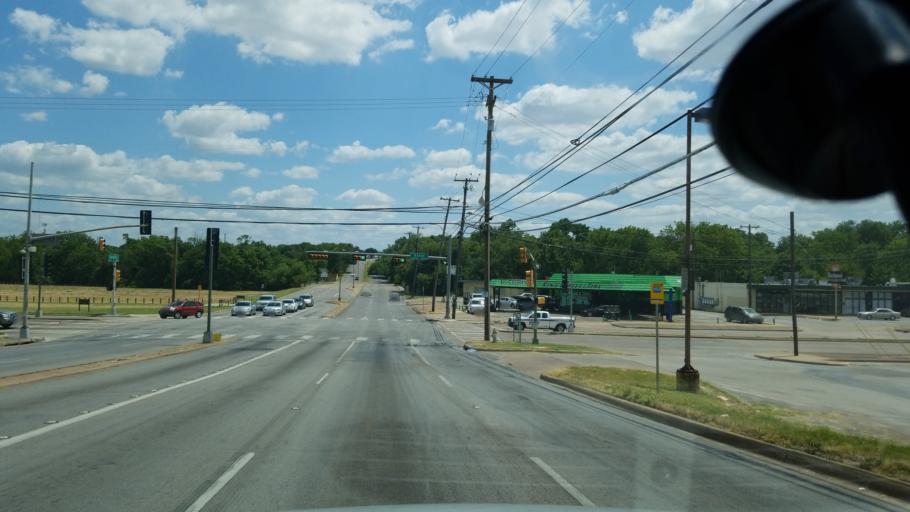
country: US
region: Texas
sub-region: Dallas County
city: Cockrell Hill
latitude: 32.7063
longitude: -96.8572
